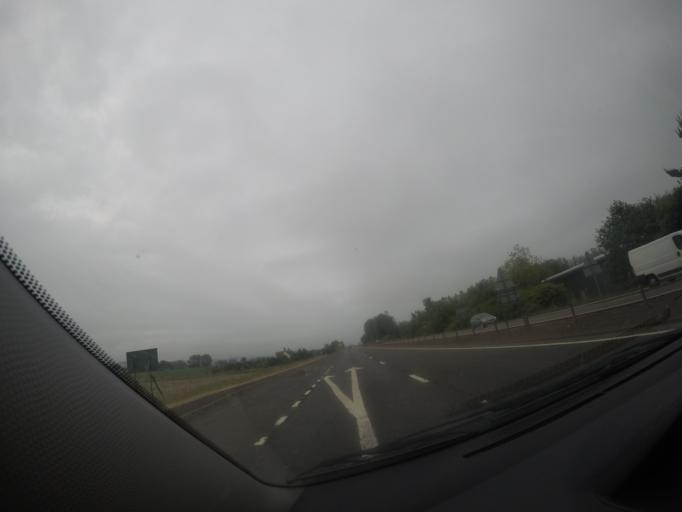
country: GB
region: Scotland
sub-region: Perth and Kinross
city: Errol
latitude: 56.4255
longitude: -3.2195
